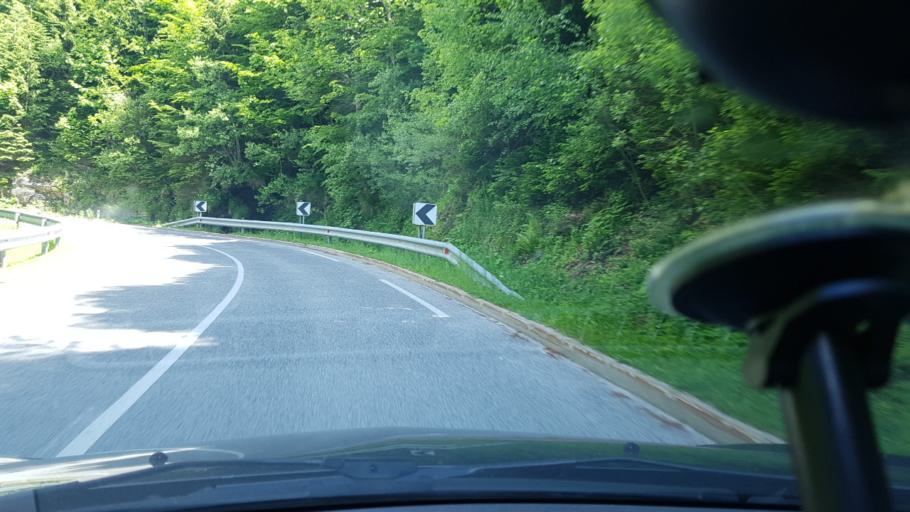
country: SI
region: Zrece
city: Zrece
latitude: 46.4375
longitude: 15.3679
